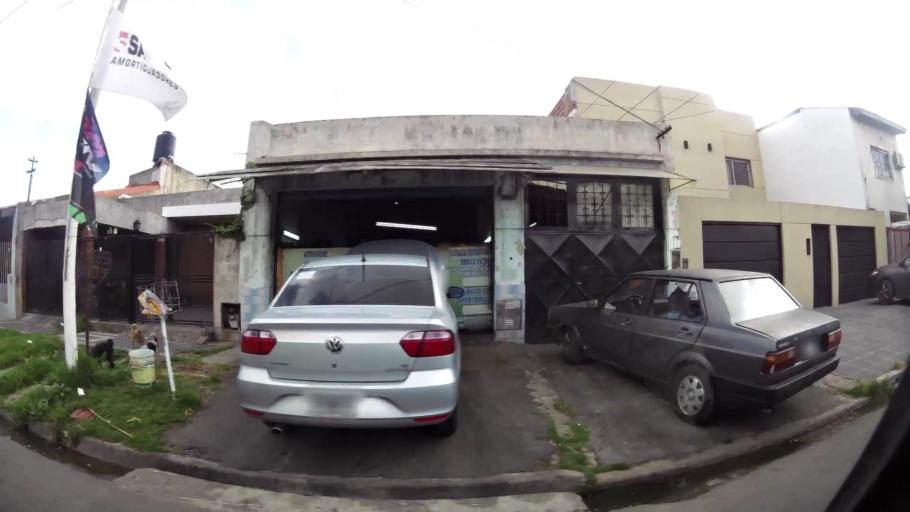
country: AR
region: Buenos Aires
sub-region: Partido de Lanus
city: Lanus
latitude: -34.6907
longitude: -58.3682
